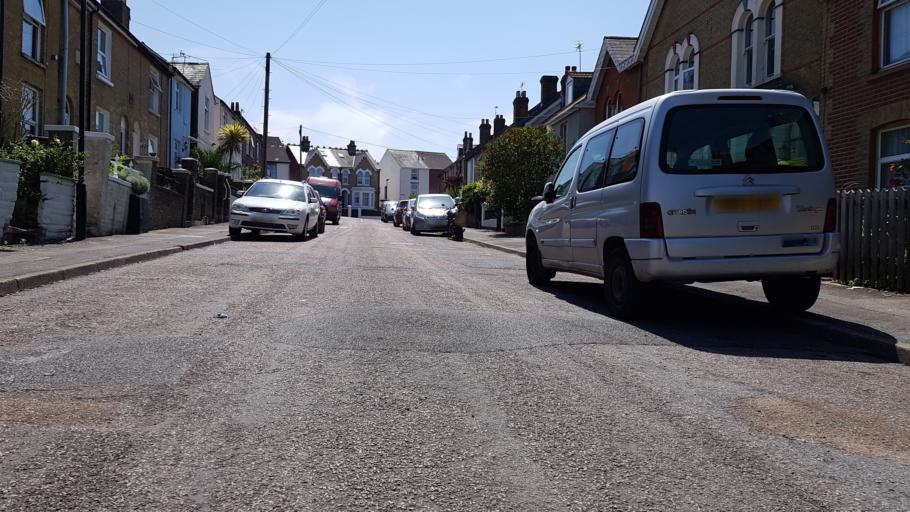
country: GB
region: England
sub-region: Isle of Wight
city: Cowes
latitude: 50.7568
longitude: -1.3024
